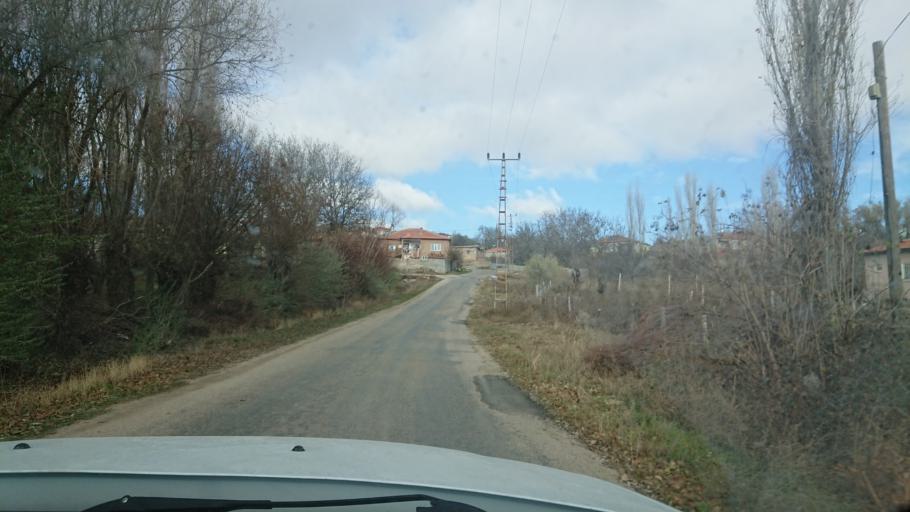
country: TR
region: Aksaray
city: Agacoren
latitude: 38.8205
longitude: 33.9593
